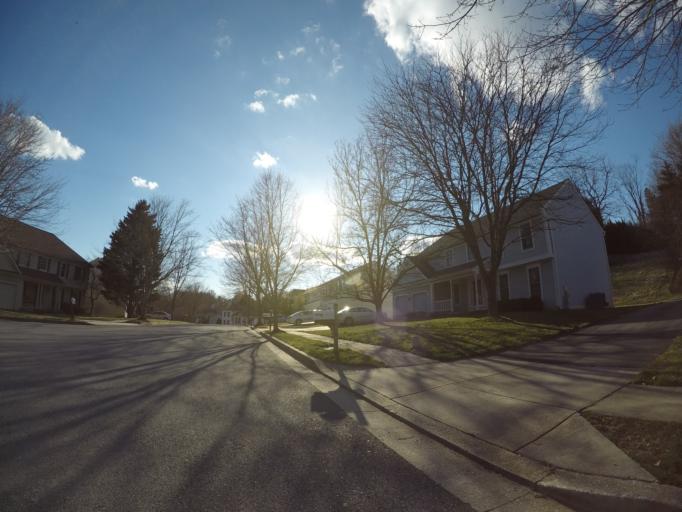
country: US
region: Maryland
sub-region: Howard County
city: Ellicott City
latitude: 39.2599
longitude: -76.8105
